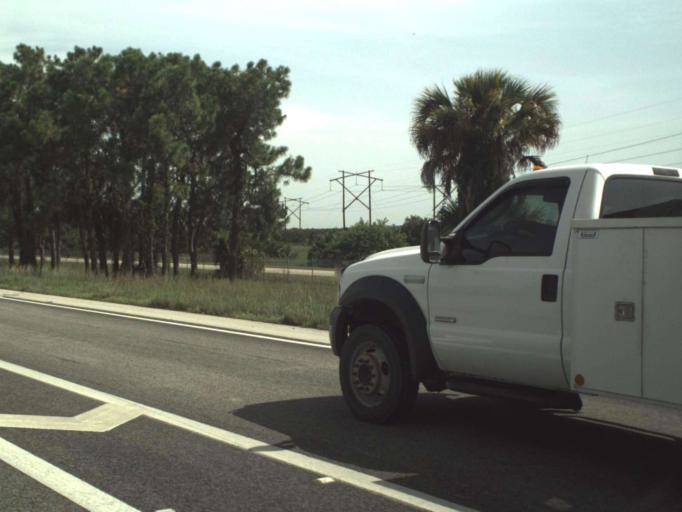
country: US
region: Florida
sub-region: Saint Lucie County
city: Lakewood Park
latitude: 27.5173
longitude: -80.4488
